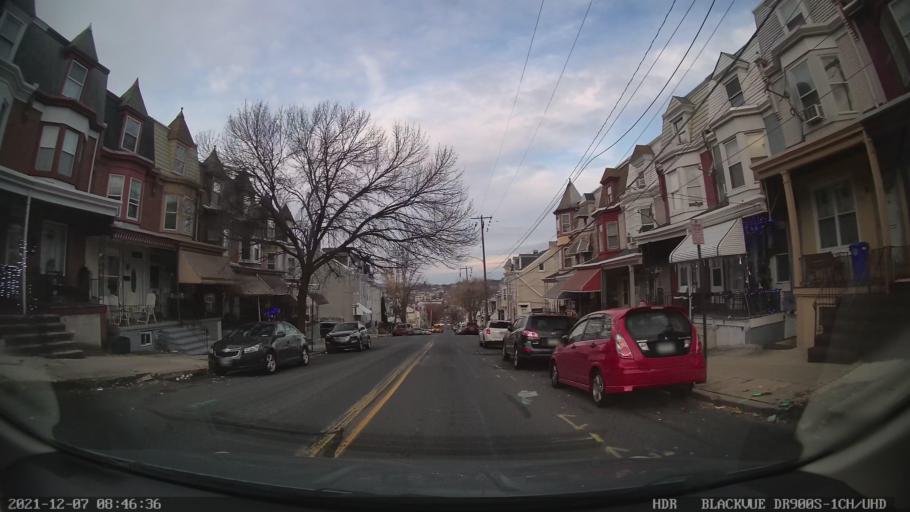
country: US
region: Pennsylvania
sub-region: Berks County
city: Reading
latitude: 40.3501
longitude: -75.9123
